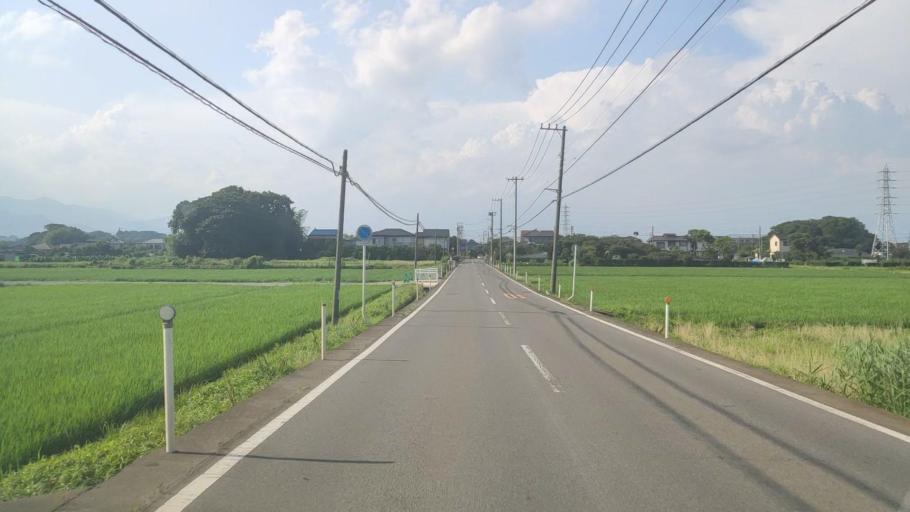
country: JP
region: Kanagawa
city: Isehara
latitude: 35.3685
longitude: 139.3285
